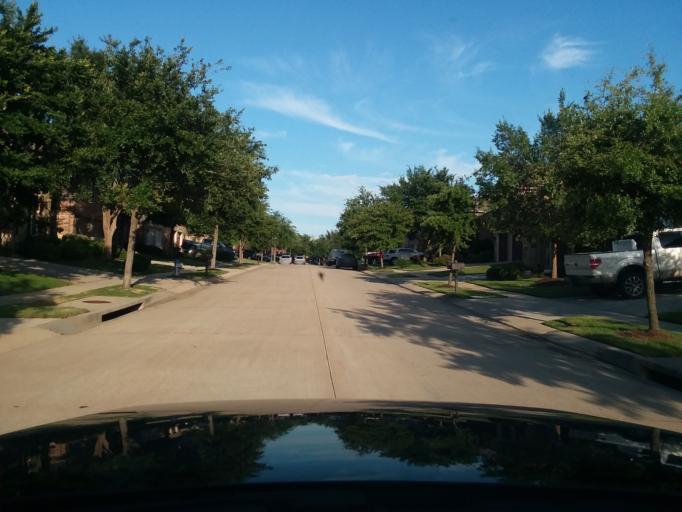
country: US
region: Texas
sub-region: Denton County
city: Copper Canyon
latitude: 33.1048
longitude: -97.1176
